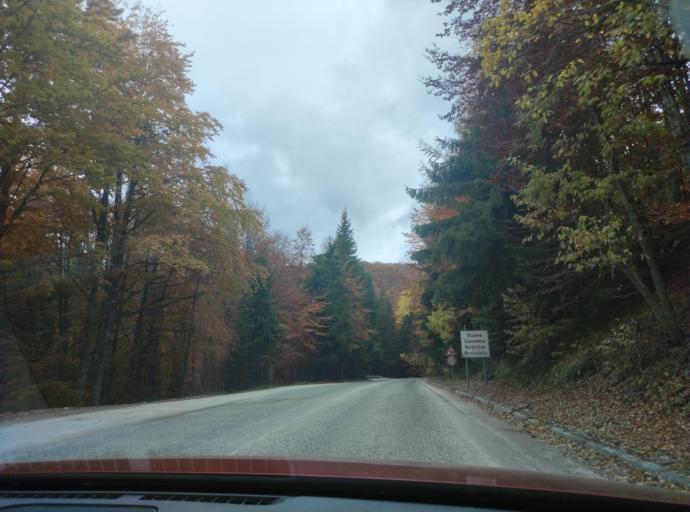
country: BG
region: Sofiya
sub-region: Obshtina Godech
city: Godech
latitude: 43.1126
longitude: 23.1124
